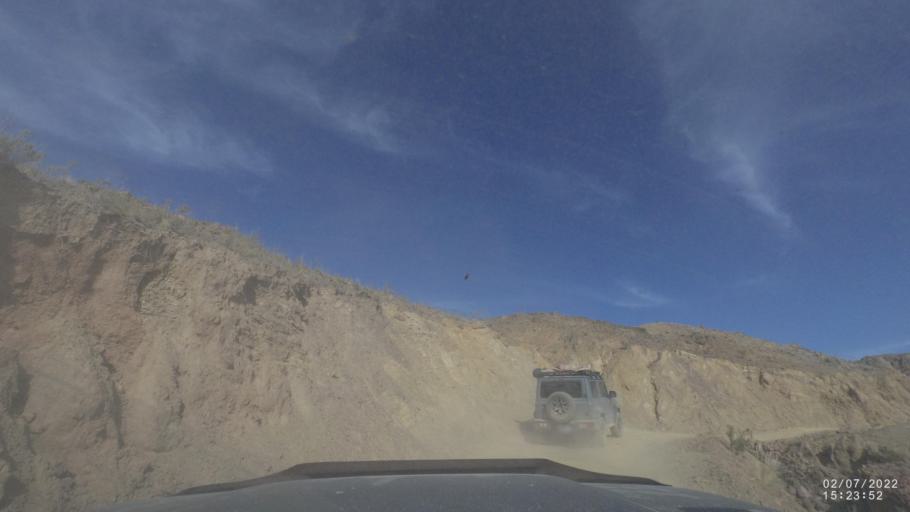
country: BO
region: Cochabamba
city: Irpa Irpa
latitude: -17.8746
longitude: -66.4184
